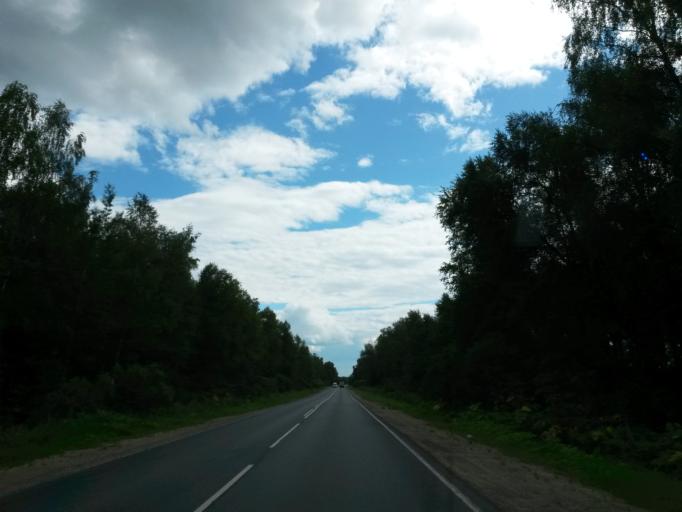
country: RU
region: Ivanovo
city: Pistsovo
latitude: 57.0745
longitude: 40.6840
